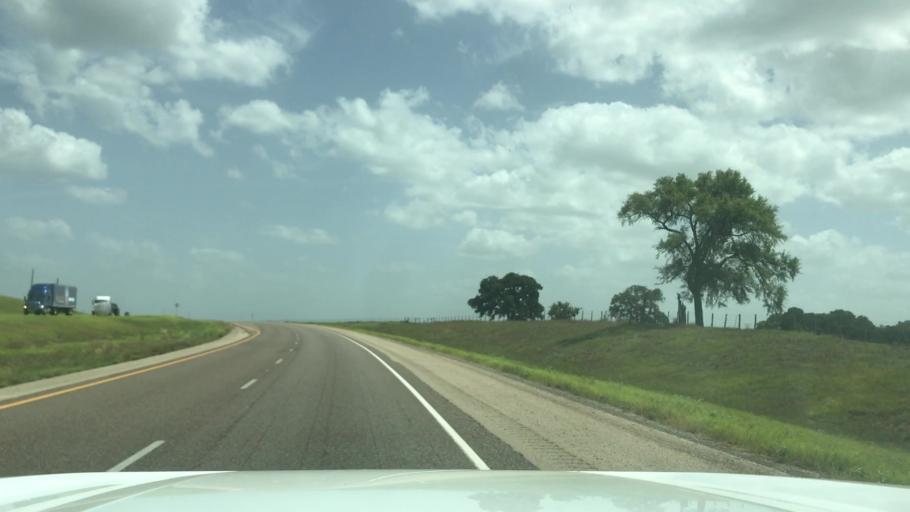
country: US
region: Texas
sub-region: Robertson County
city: Calvert
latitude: 31.0088
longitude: -96.7021
